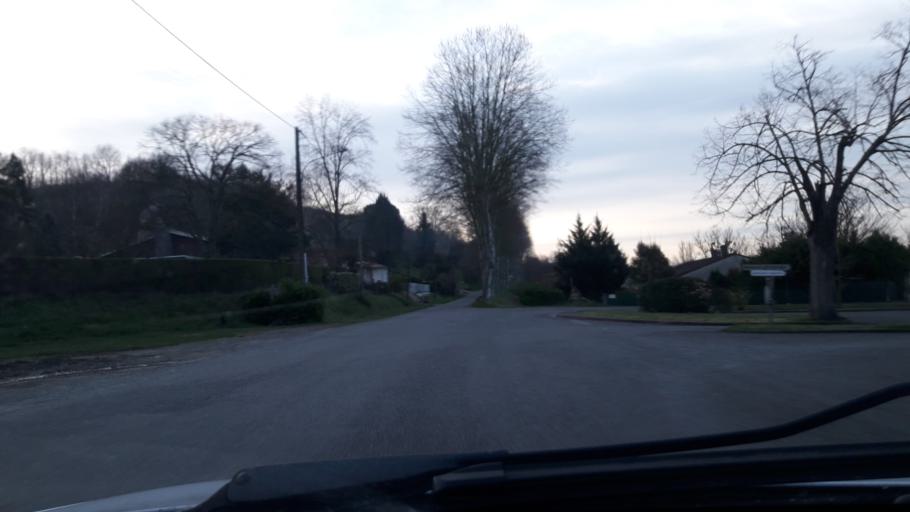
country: FR
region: Midi-Pyrenees
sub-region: Departement de la Haute-Garonne
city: Montesquieu-Volvestre
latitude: 43.2064
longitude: 1.2337
